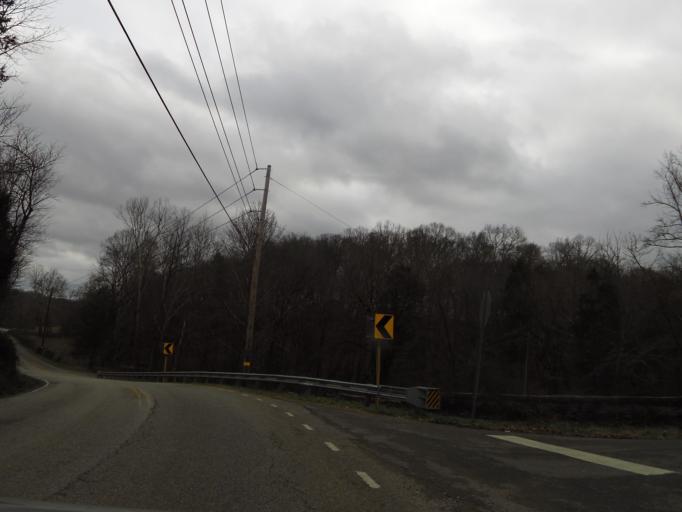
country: US
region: Tennessee
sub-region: Grainger County
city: Rutledge
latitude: 36.2057
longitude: -83.5556
